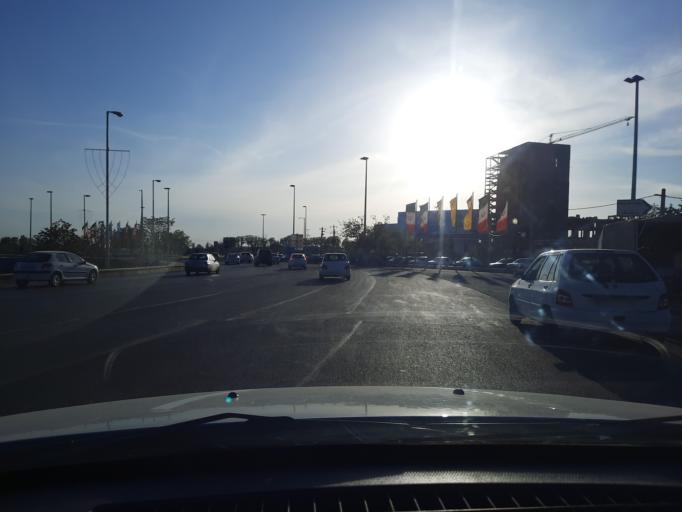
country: IR
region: Qazvin
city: Qazvin
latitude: 36.2625
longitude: 50.0473
